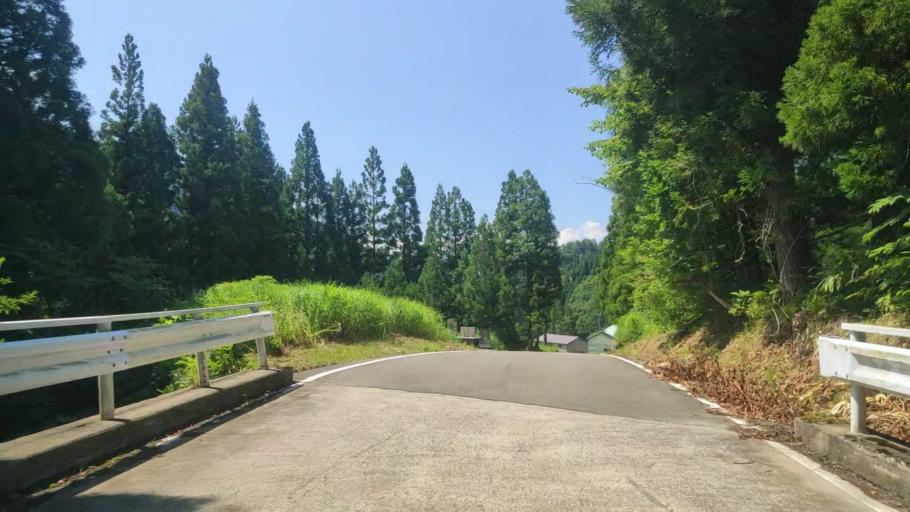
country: JP
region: Fukui
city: Katsuyama
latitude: 36.1262
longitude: 136.5085
